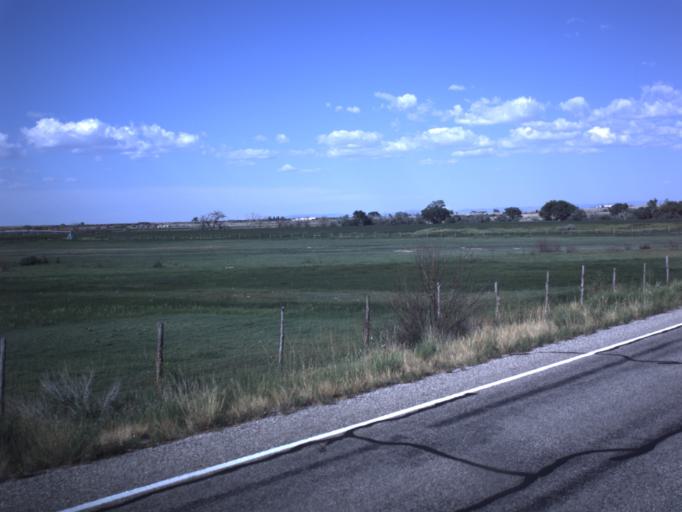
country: US
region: Utah
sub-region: Emery County
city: Huntington
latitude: 39.3449
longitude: -110.9336
